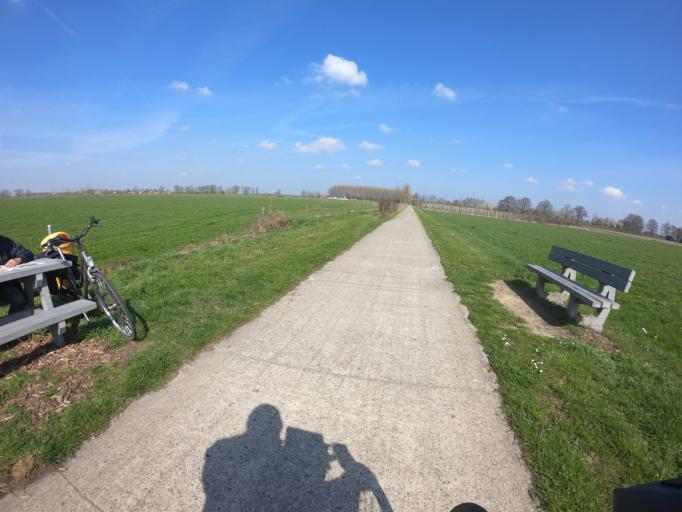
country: BE
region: Flanders
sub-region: Provincie Vlaams-Brabant
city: Geetbets
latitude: 50.9121
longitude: 5.1122
